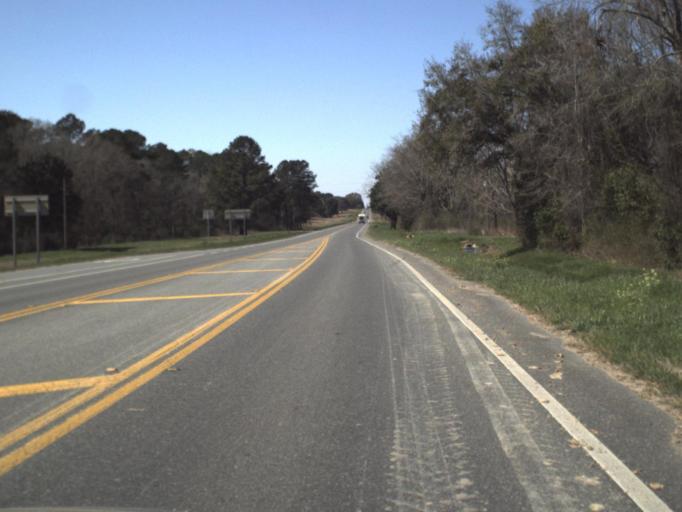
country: US
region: Florida
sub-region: Jackson County
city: Marianna
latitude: 30.7846
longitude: -85.2968
